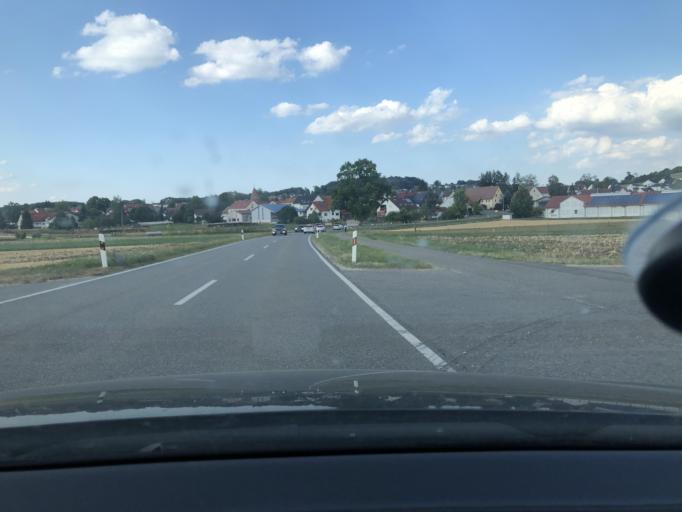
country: DE
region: Baden-Wuerttemberg
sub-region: Tuebingen Region
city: Pfullingen
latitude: 48.4019
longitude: 9.1824
